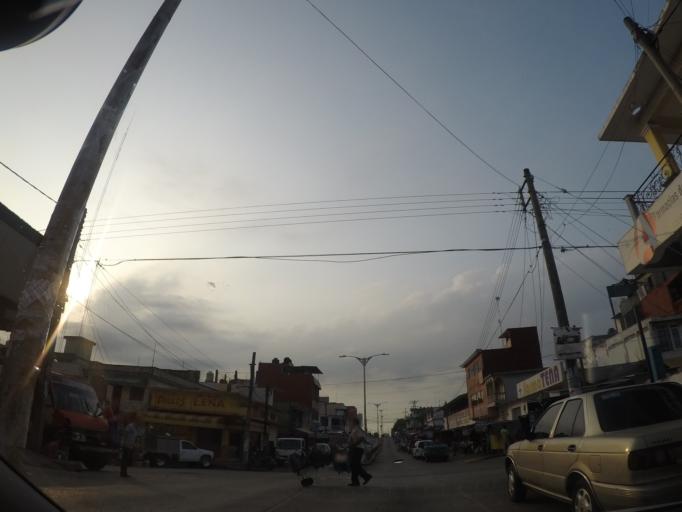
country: MX
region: Oaxaca
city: Matias Romero
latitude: 16.8788
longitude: -95.0413
